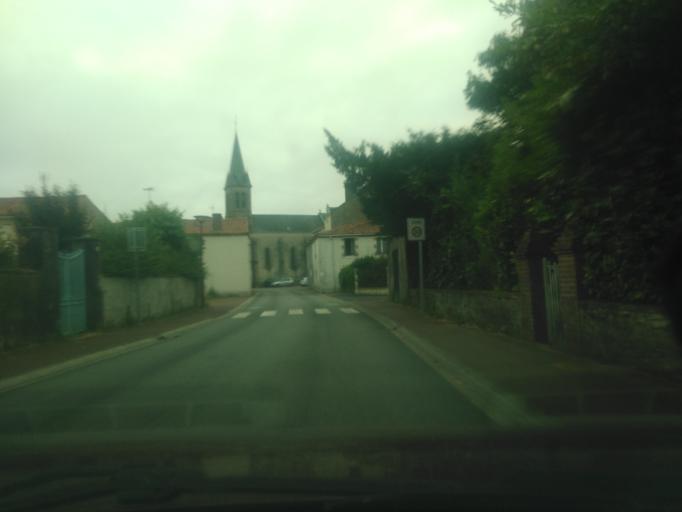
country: FR
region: Pays de la Loire
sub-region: Departement de la Vendee
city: La Ferriere
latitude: 46.7682
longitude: -1.3016
